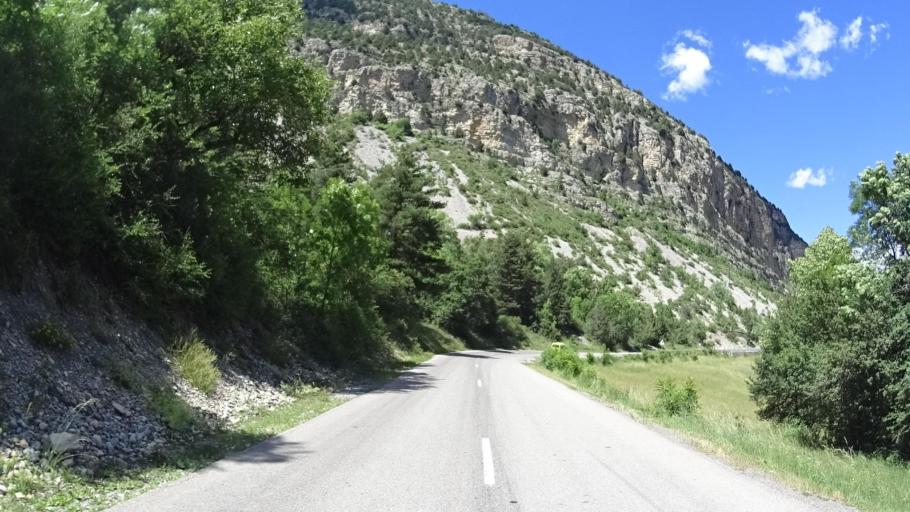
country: FR
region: Provence-Alpes-Cote d'Azur
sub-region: Departement des Alpes-de-Haute-Provence
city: Annot
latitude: 44.1020
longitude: 6.5688
